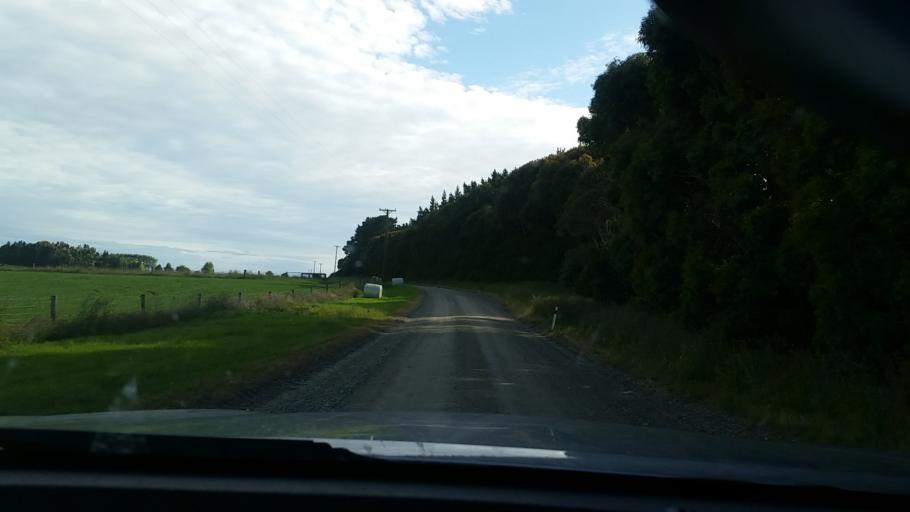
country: NZ
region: Southland
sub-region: Gore District
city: Gore
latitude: -46.2538
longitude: 168.7477
